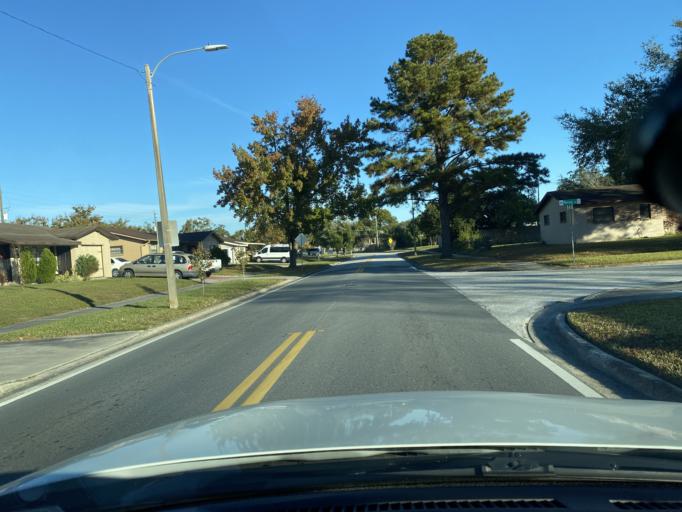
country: US
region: Florida
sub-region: Orange County
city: Azalea Park
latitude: 28.5297
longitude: -81.2988
